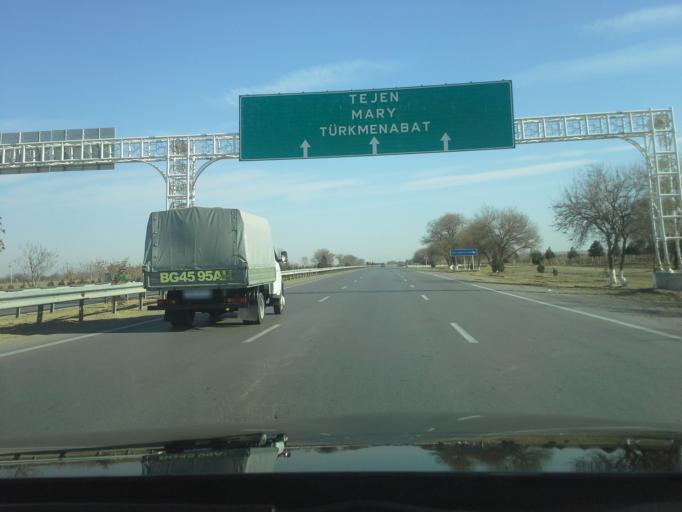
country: TM
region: Ahal
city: Annau
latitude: 37.9037
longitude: 58.5493
